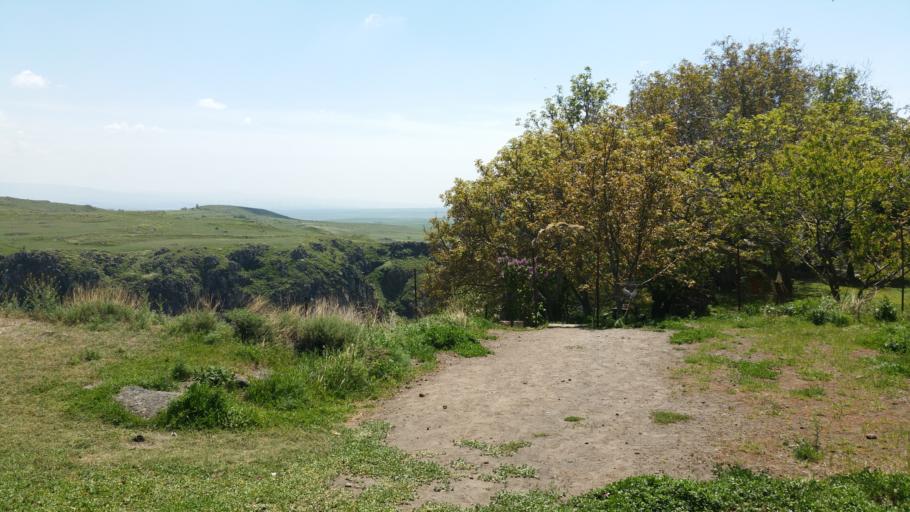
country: AM
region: Aragatsotn
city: Ushi
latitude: 40.3805
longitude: 44.3966
